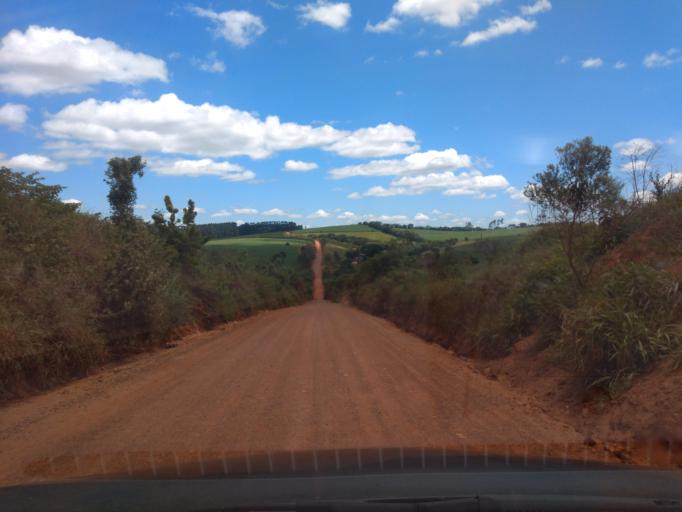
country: BR
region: Minas Gerais
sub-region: Lavras
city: Lavras
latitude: -21.5429
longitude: -44.9857
